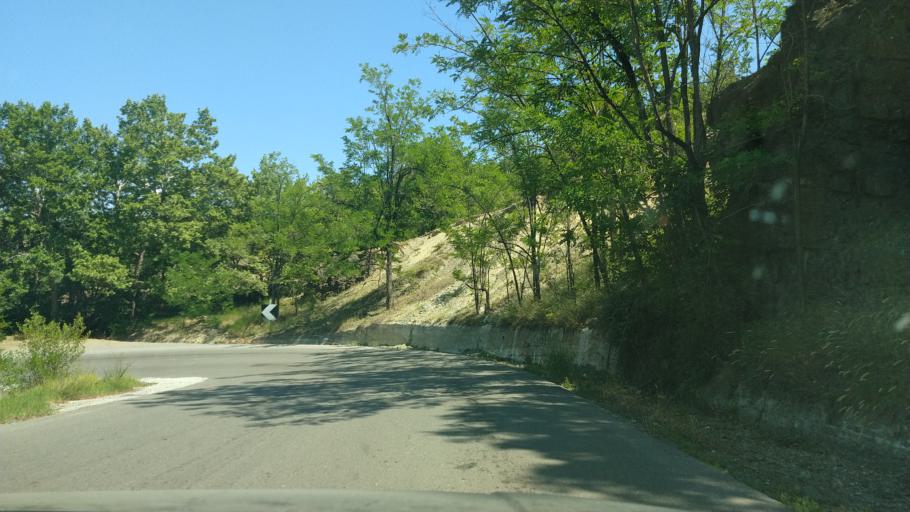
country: GR
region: West Macedonia
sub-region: Nomos Grevenon
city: Grevena
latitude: 40.0494
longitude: 21.4832
